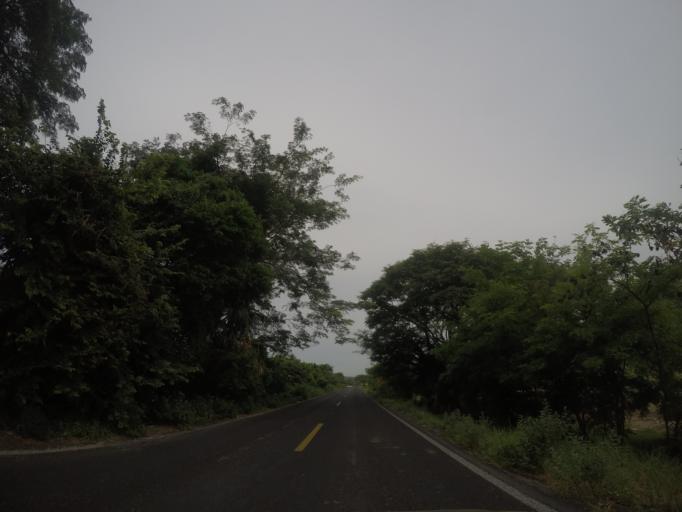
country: MX
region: Oaxaca
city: San Pedro Mixtepec
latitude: 15.9562
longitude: -97.2399
